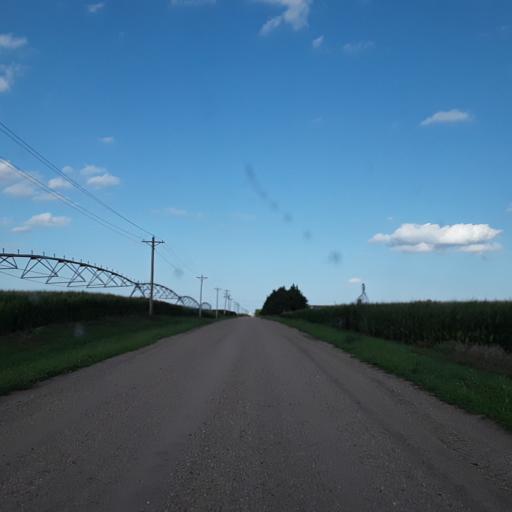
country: US
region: Nebraska
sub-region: Hall County
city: Wood River
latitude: 40.9168
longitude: -98.5585
